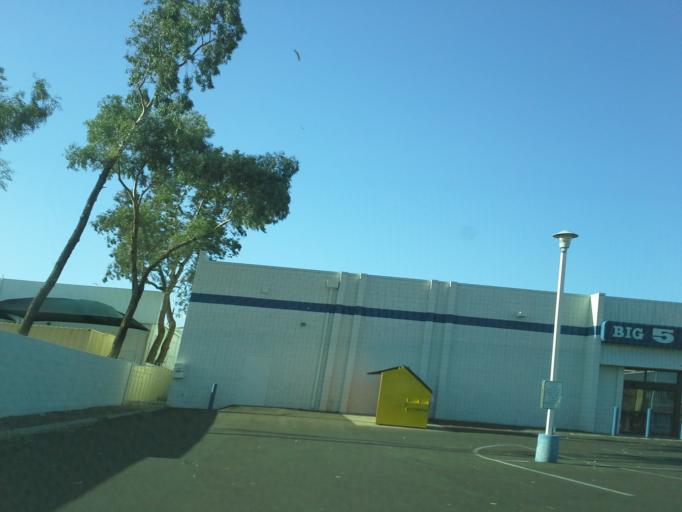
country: US
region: Arizona
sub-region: Maricopa County
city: Glendale
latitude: 33.6392
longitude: -112.1009
